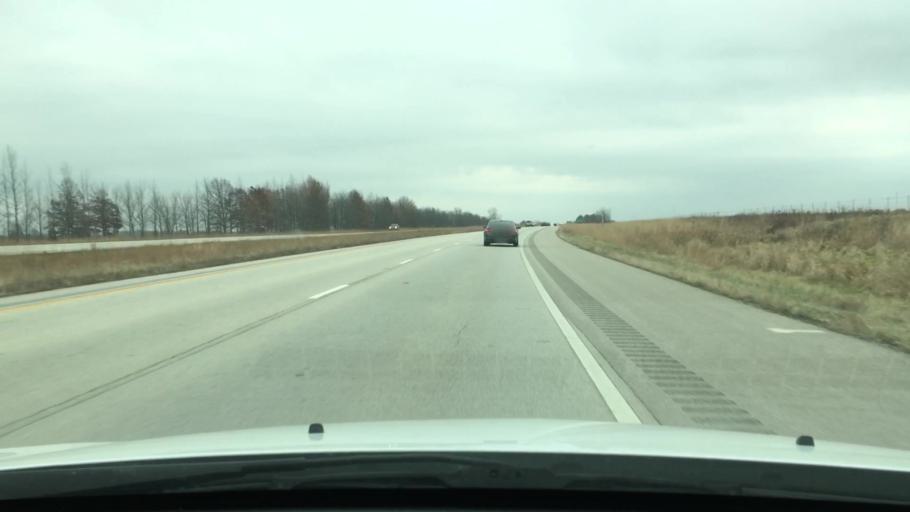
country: US
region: Illinois
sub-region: Sangamon County
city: New Berlin
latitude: 39.7515
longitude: -89.7969
